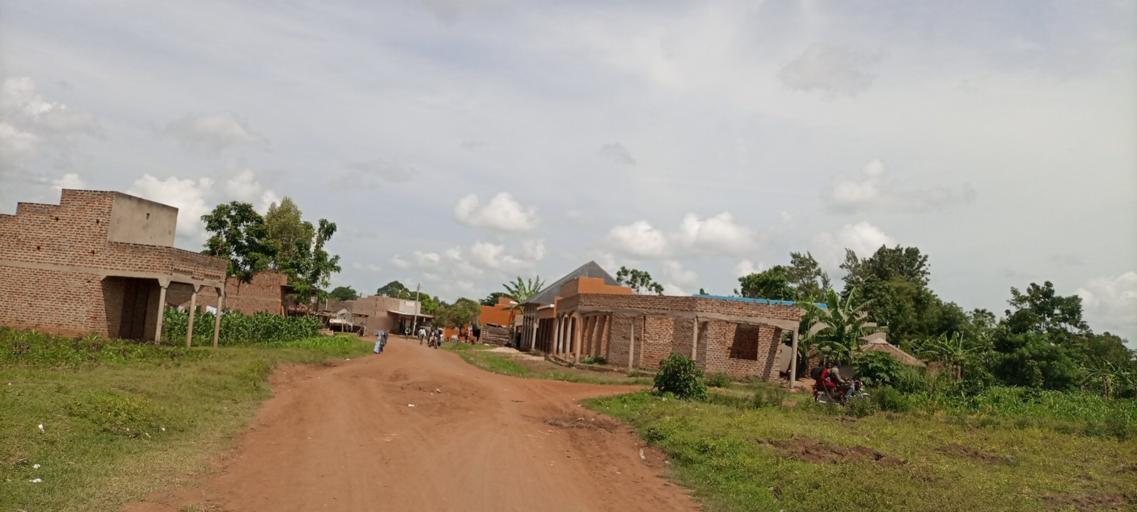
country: UG
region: Eastern Region
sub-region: Budaka District
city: Budaka
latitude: 1.1725
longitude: 33.9346
